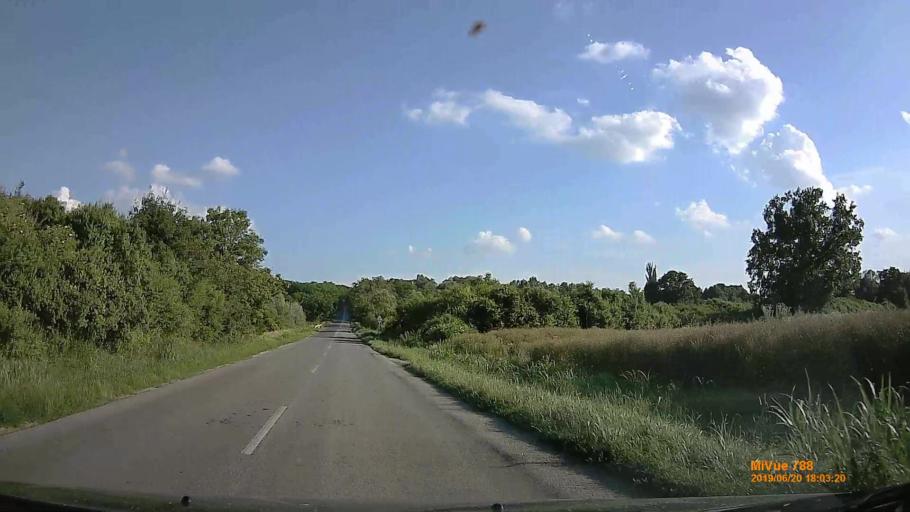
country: HU
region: Baranya
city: Szentlorinc
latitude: 46.0629
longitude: 17.9908
